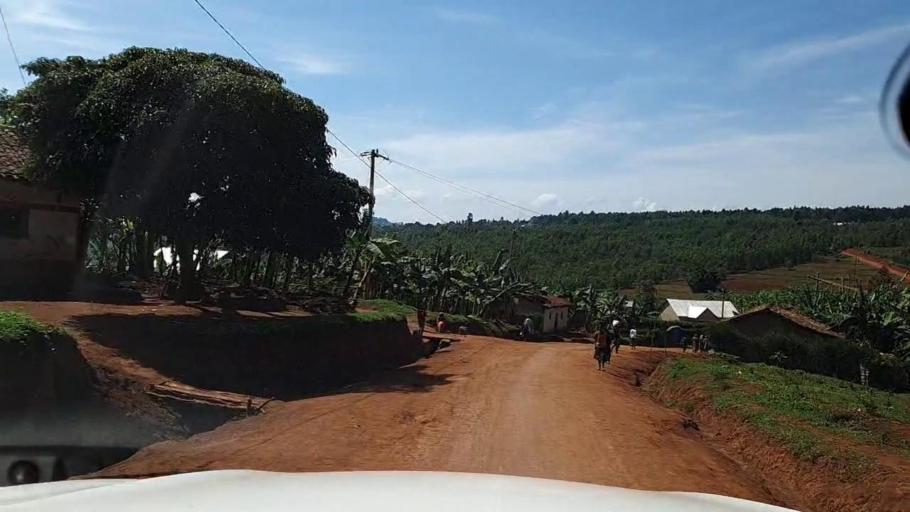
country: RW
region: Southern Province
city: Butare
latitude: -2.6982
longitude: 29.8547
